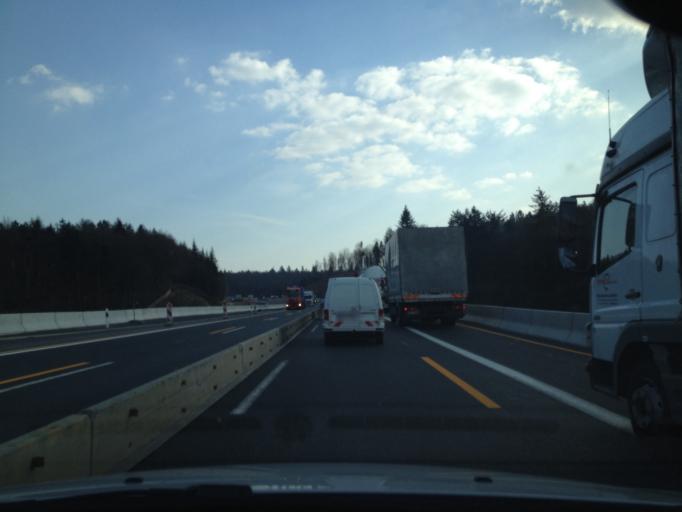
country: DE
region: Bavaria
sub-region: Regierungsbezirk Unterfranken
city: Weibersbrunn
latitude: 49.9264
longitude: 9.3539
